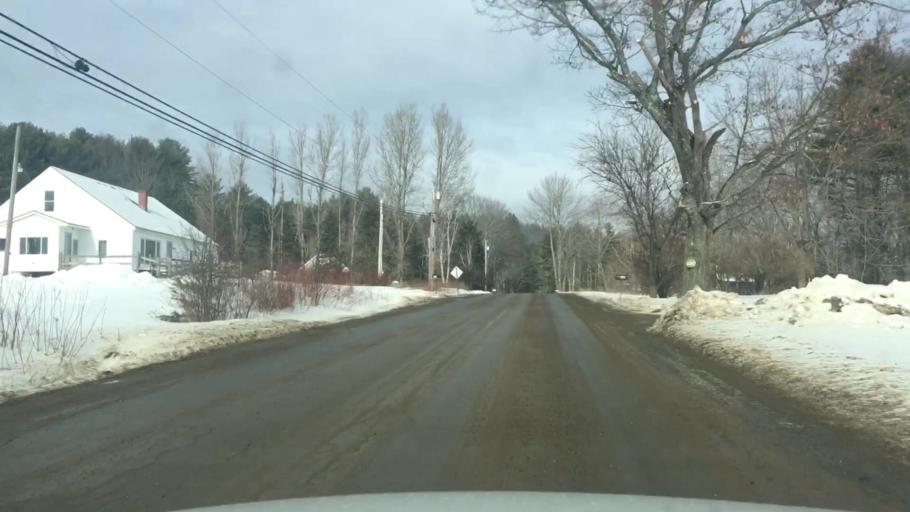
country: US
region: Maine
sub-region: Penobscot County
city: Hermon
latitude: 44.7692
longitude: -68.9605
